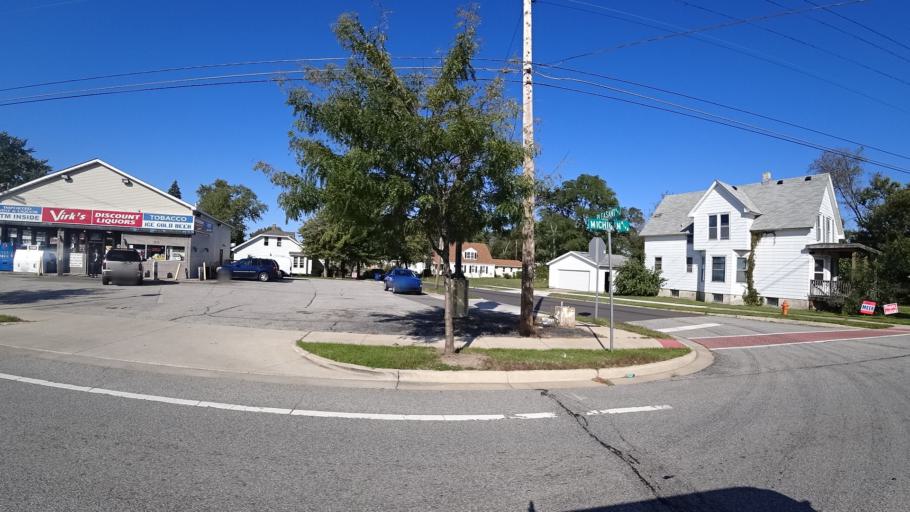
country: US
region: Indiana
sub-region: LaPorte County
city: Trail Creek
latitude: 41.7098
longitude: -86.8739
